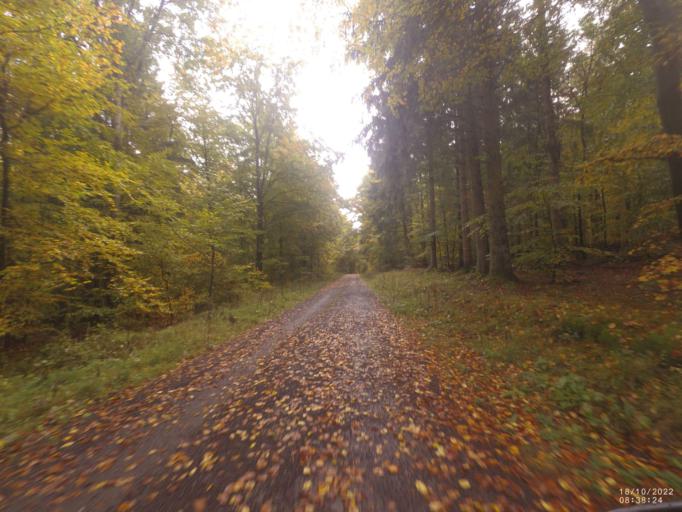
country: DE
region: Rheinland-Pfalz
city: Daun
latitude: 50.2253
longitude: 6.8171
